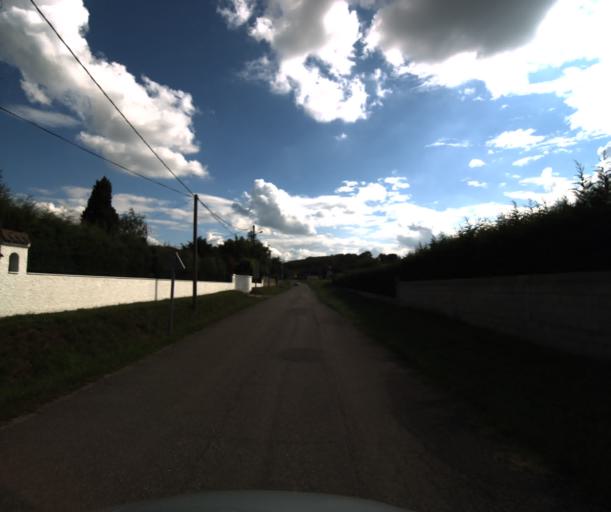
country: FR
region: Midi-Pyrenees
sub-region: Departement de la Haute-Garonne
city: Saubens
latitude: 43.4782
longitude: 1.3532
